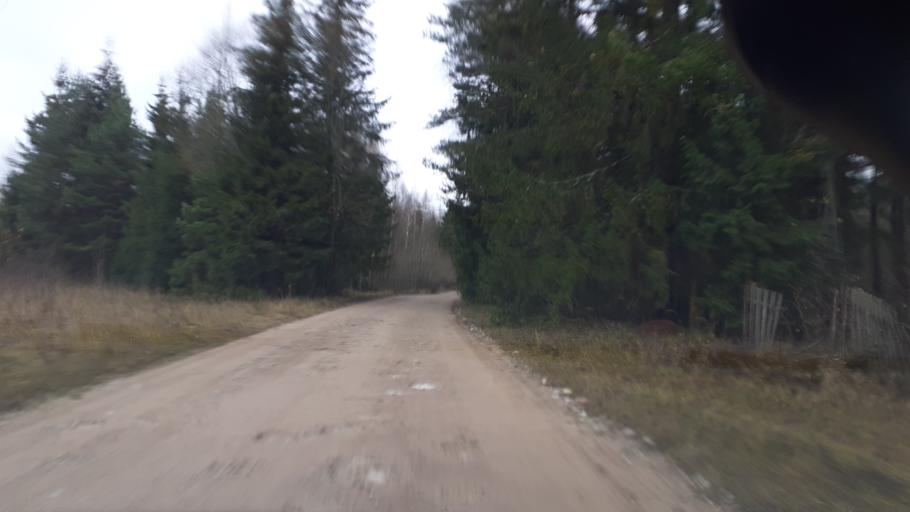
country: LV
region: Kuldigas Rajons
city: Kuldiga
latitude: 57.0277
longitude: 21.8696
